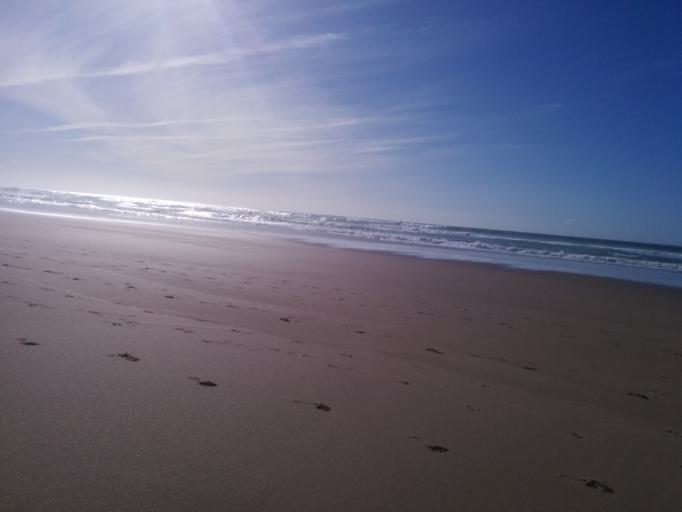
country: PT
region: Faro
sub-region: Vila do Bispo
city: Vila do Bispo
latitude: 37.2081
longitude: -8.8947
